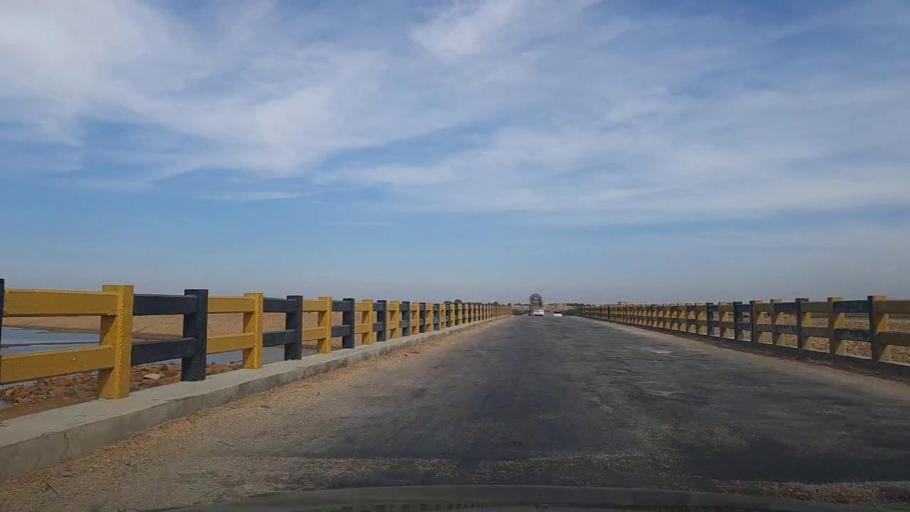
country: PK
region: Sindh
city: Daro Mehar
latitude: 24.9044
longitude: 68.0688
